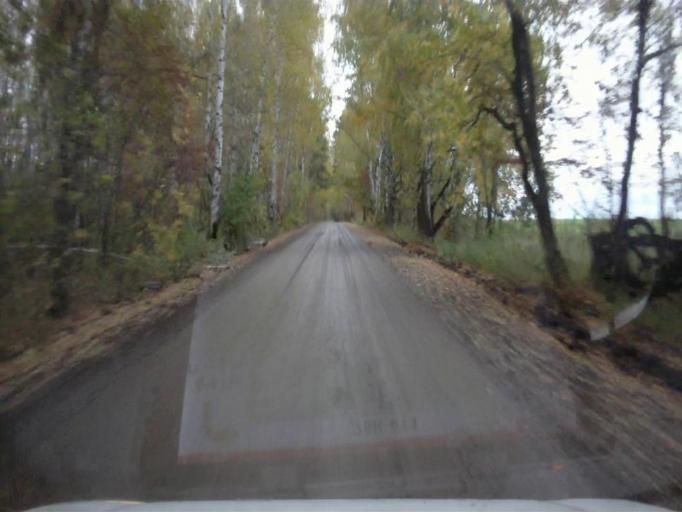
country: RU
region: Sverdlovsk
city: Mikhaylovsk
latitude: 56.1705
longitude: 59.2237
